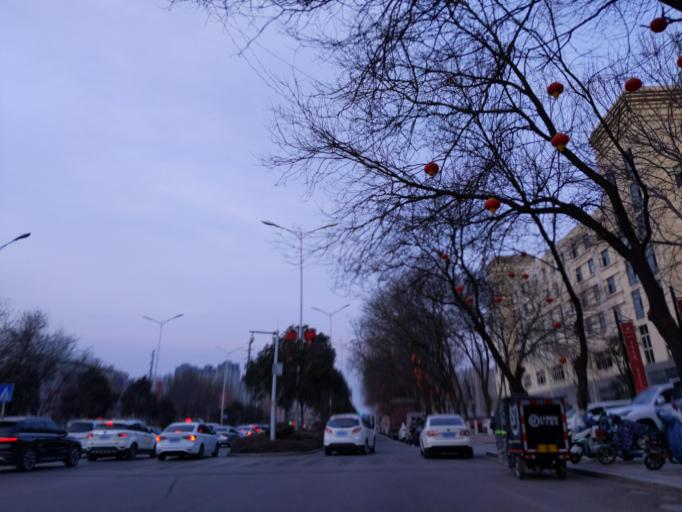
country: CN
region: Henan Sheng
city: Puyang
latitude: 35.7792
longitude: 115.0207
